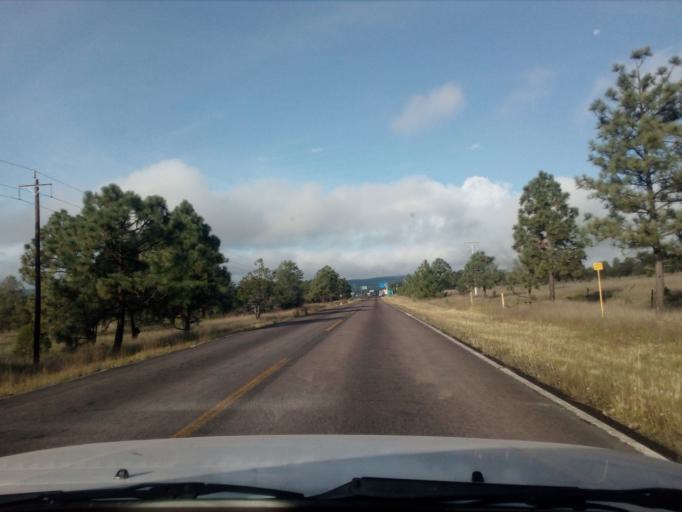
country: MX
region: Durango
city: Victoria de Durango
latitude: 23.9259
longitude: -104.9363
